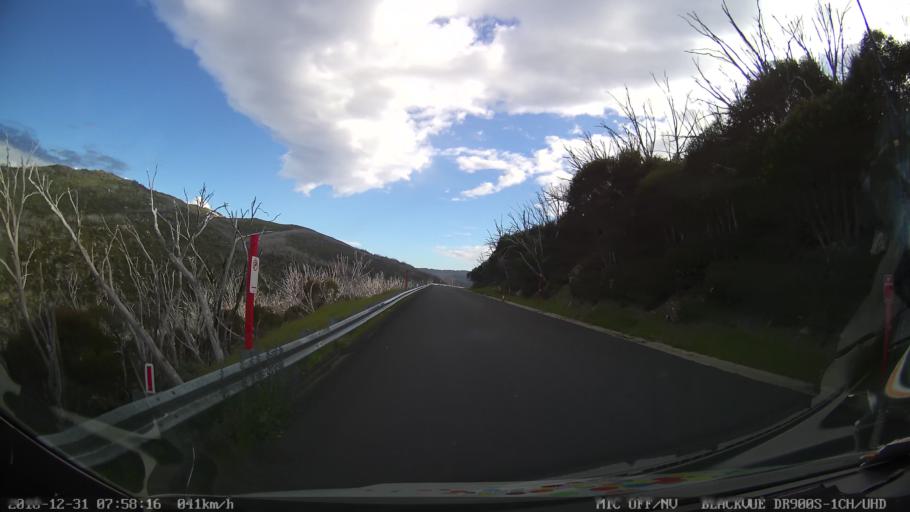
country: AU
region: New South Wales
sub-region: Snowy River
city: Jindabyne
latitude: -36.3757
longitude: 148.3786
